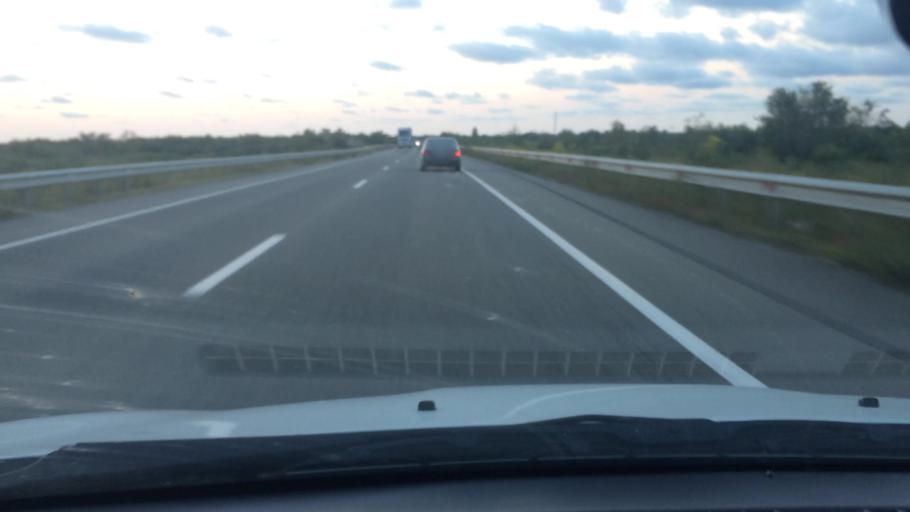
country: GE
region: Ajaria
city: Ochkhamuri
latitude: 41.9059
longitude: 41.7881
